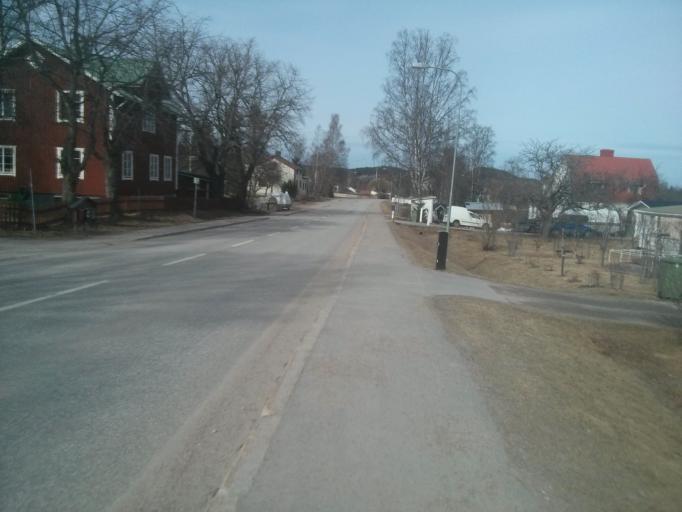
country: SE
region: Vaesternorrland
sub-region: Sundsvalls Kommun
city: Njurundabommen
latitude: 62.2615
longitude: 17.3772
